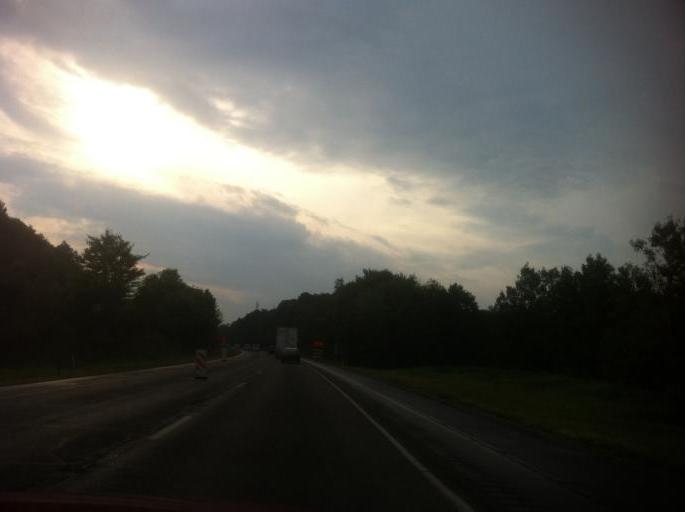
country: US
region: Pennsylvania
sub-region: Clarion County
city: Knox
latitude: 41.1943
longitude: -79.5709
